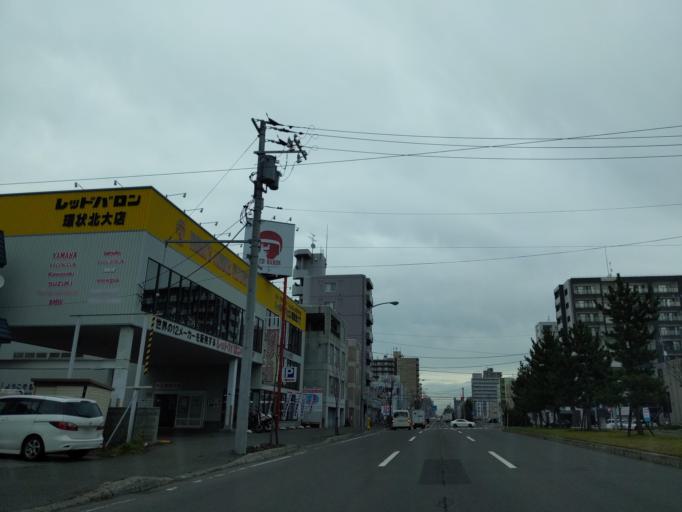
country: JP
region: Hokkaido
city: Sapporo
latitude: 43.0783
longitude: 141.3478
